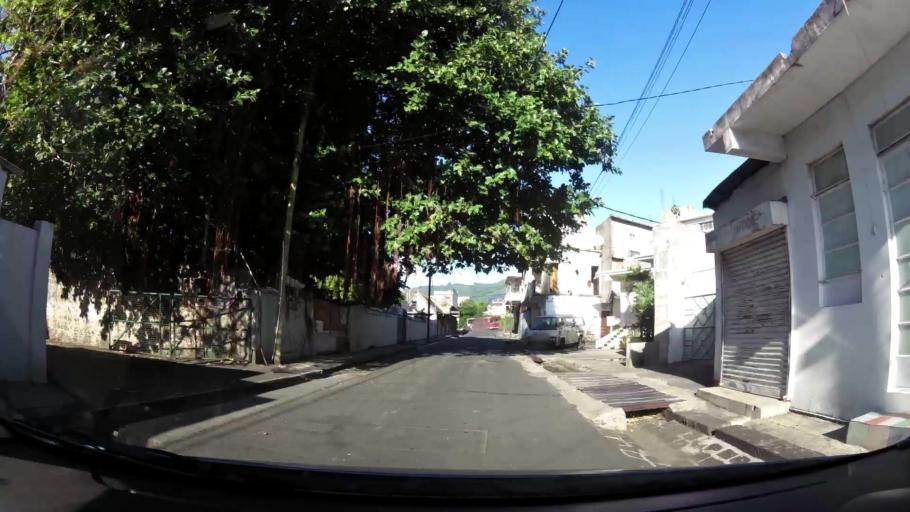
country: MU
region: Port Louis
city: Port Louis
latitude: -20.1651
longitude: 57.4909
